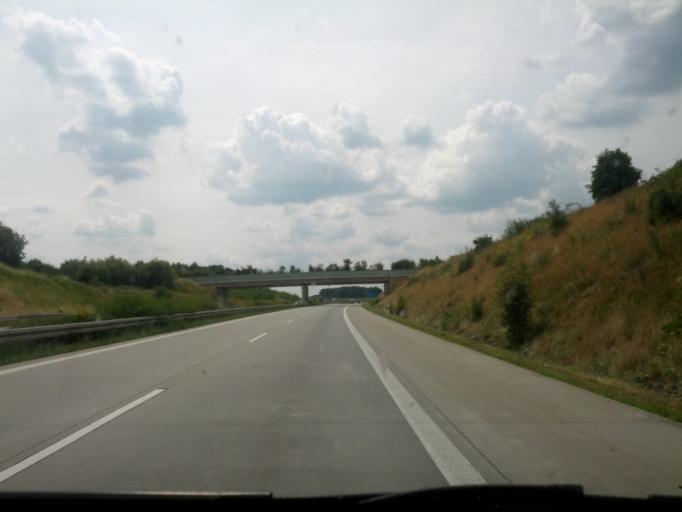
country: DE
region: Saxony
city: Liebstadt
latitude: 50.8931
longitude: 13.8872
